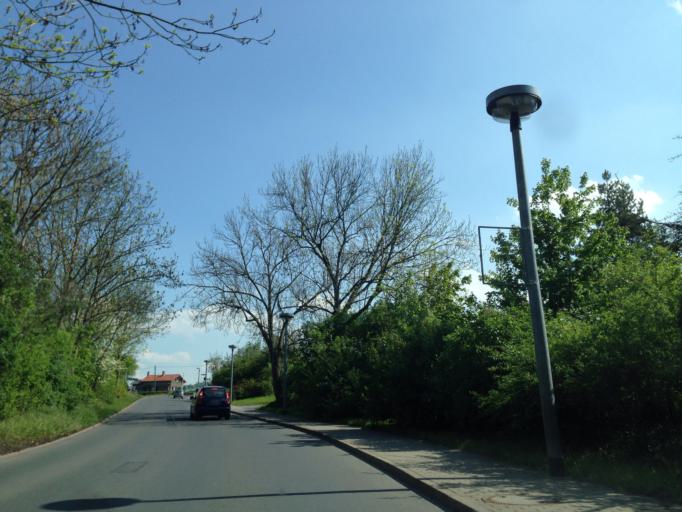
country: DE
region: Thuringia
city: Bodelwitz
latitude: 50.6969
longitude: 11.6164
